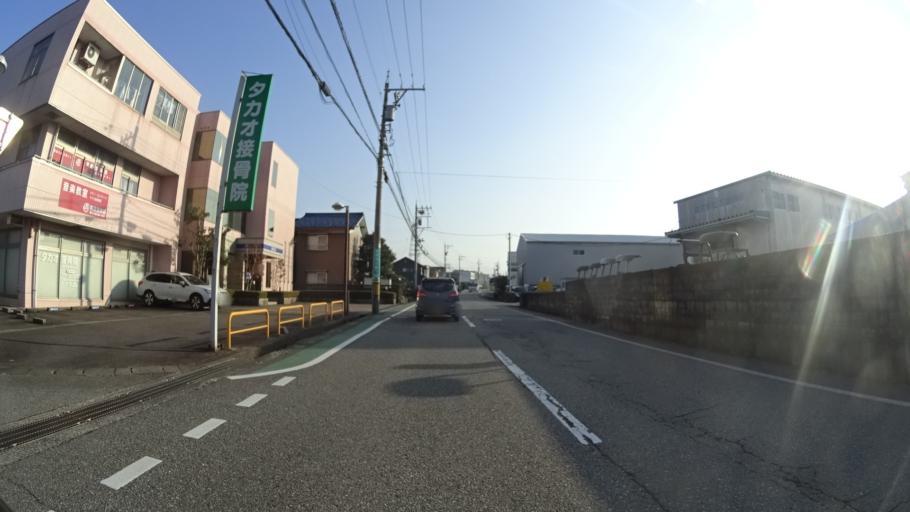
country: JP
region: Toyama
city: Kamiichi
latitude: 36.6521
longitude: 137.3132
